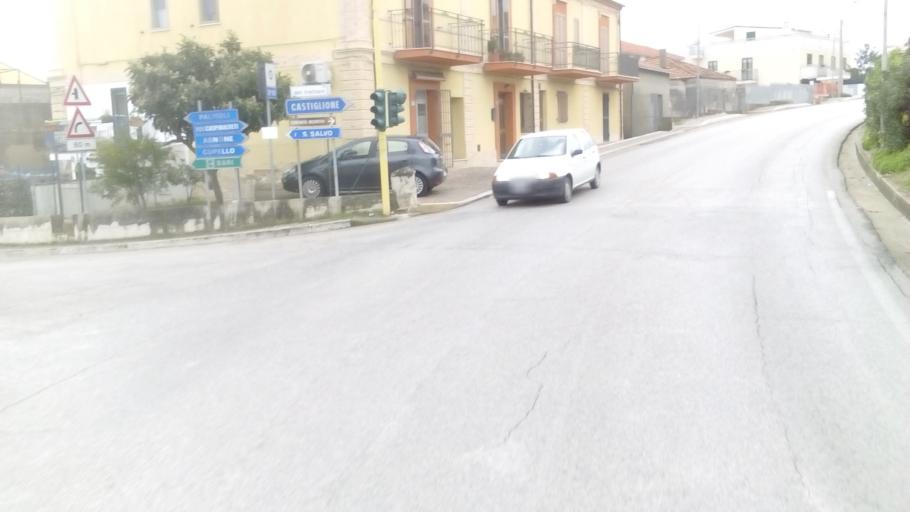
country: IT
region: Abruzzo
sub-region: Provincia di Chieti
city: Vasto
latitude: 42.0970
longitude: 14.6966
